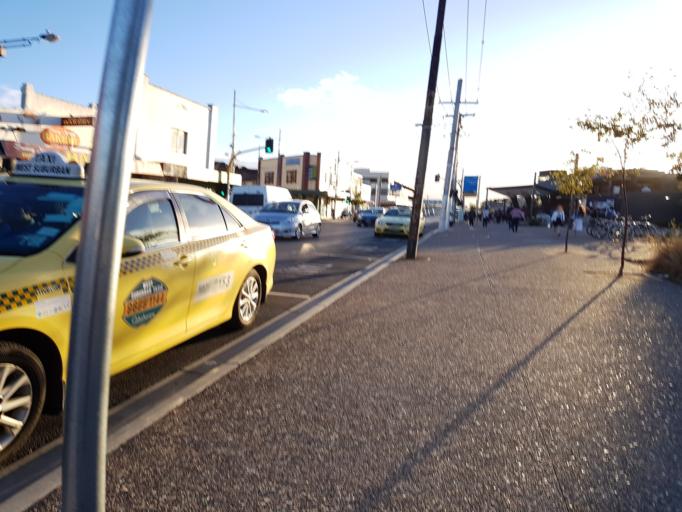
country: AU
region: Victoria
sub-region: Maribyrnong
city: Footscray
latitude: -37.8019
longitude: 144.9004
